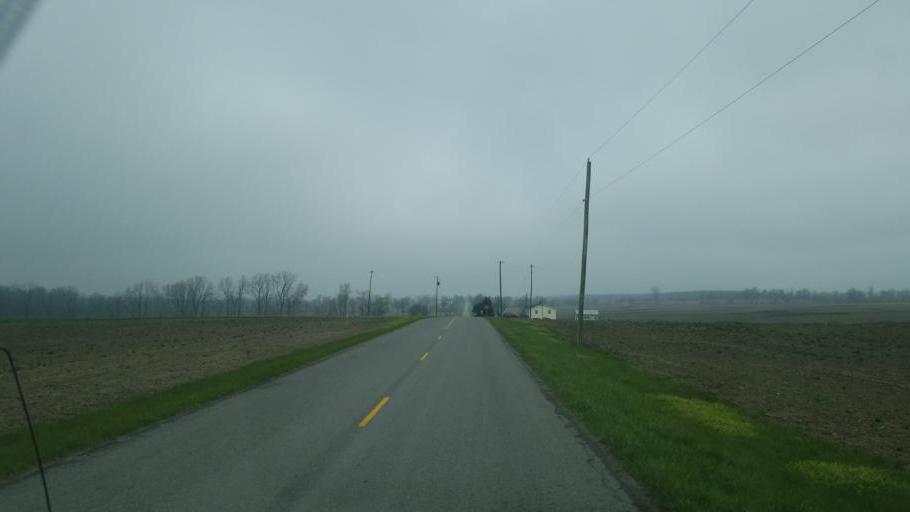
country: US
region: Ohio
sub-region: Logan County
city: Northwood
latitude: 40.5046
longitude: -83.6772
